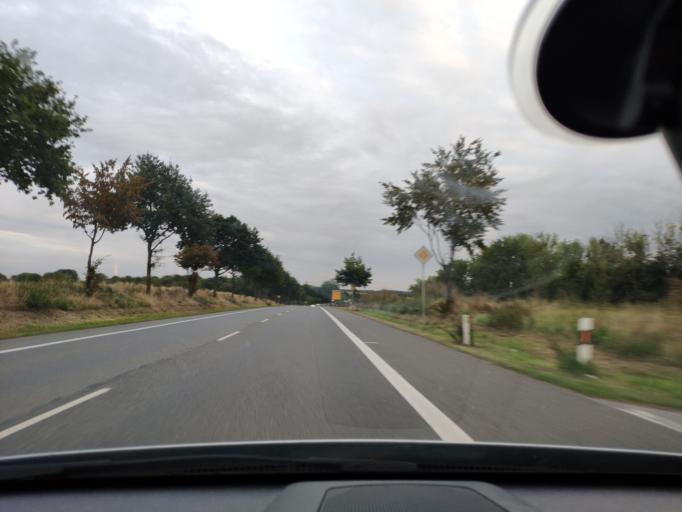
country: DE
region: North Rhine-Westphalia
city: Siersdorf
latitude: 50.9274
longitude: 6.2364
